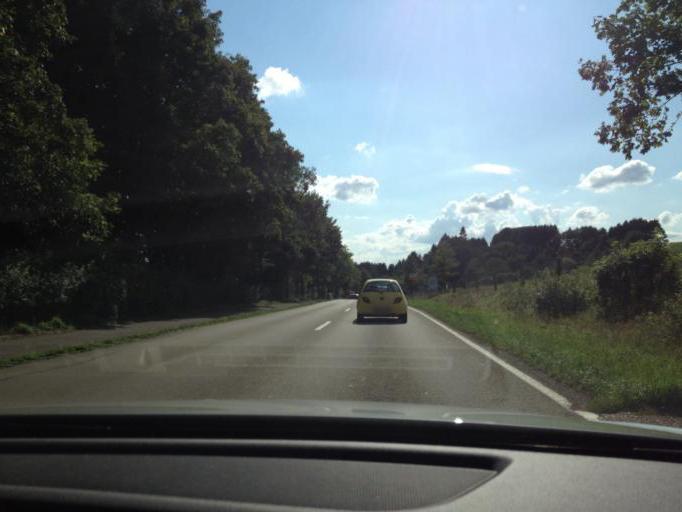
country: DE
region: Saarland
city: Illingen
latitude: 49.3957
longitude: 7.0784
